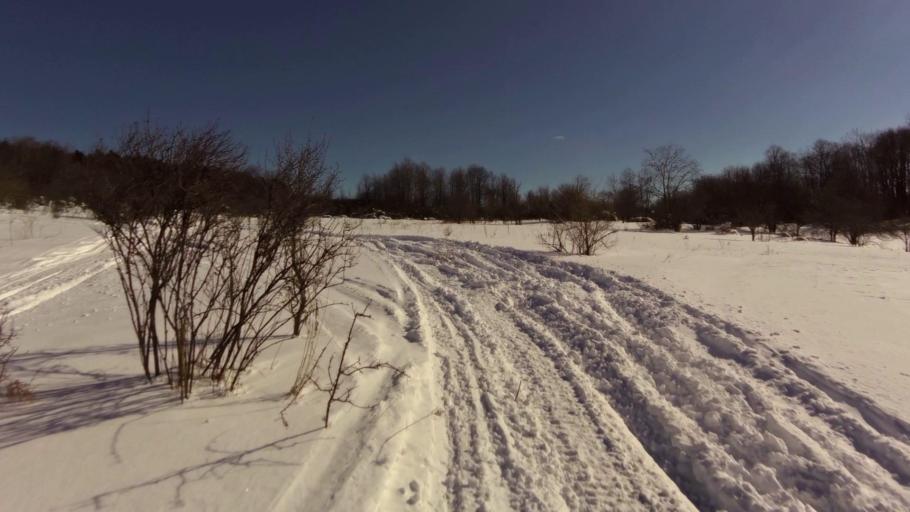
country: US
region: New York
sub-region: Cattaraugus County
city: Franklinville
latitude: 42.3461
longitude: -78.4334
